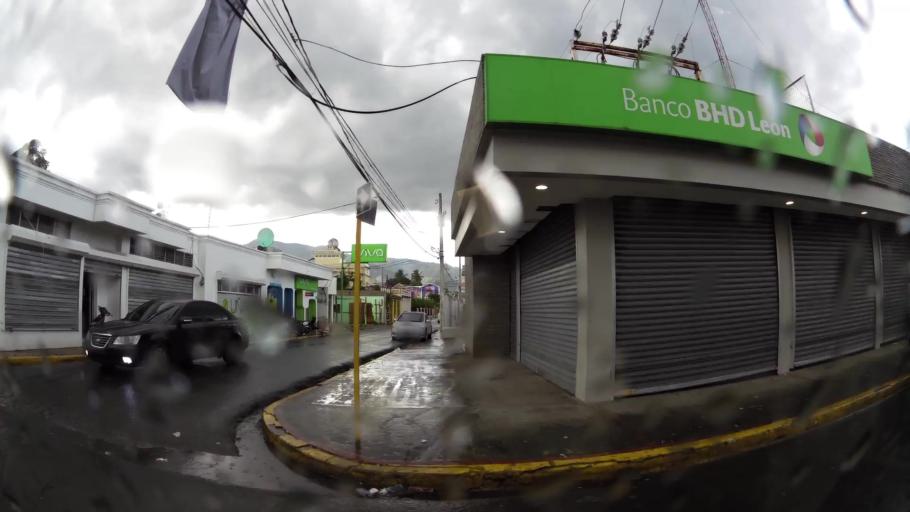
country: DO
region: Monsenor Nouel
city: Bonao
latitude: 18.9426
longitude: -70.4108
